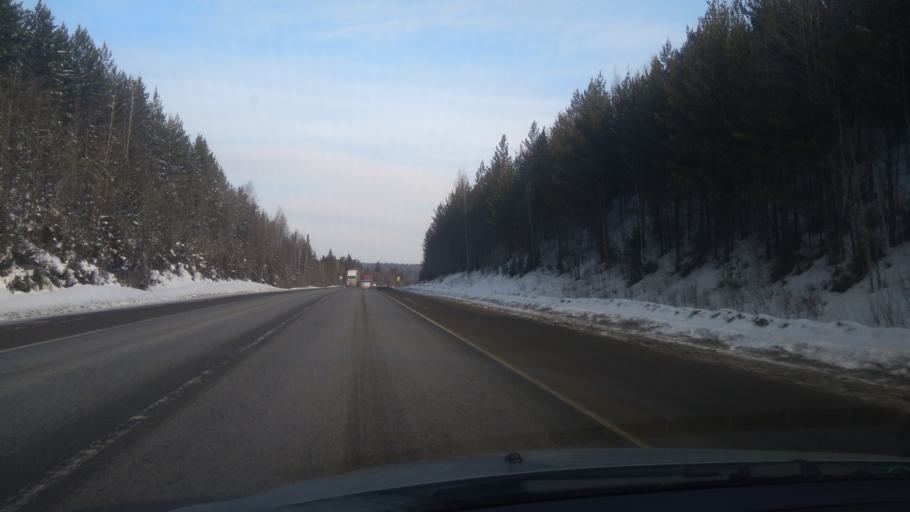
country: RU
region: Sverdlovsk
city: Revda
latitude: 56.8367
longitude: 59.8327
